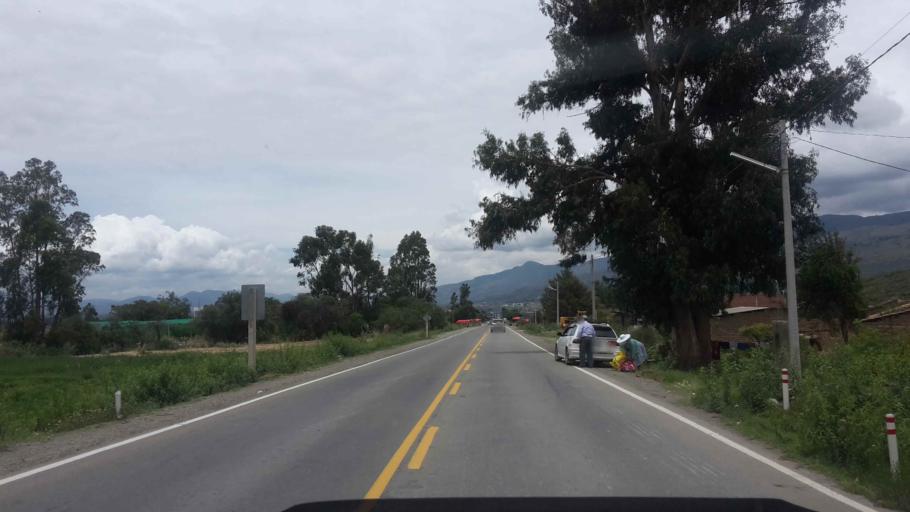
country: BO
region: Cochabamba
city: Punata
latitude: -17.5152
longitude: -65.8200
